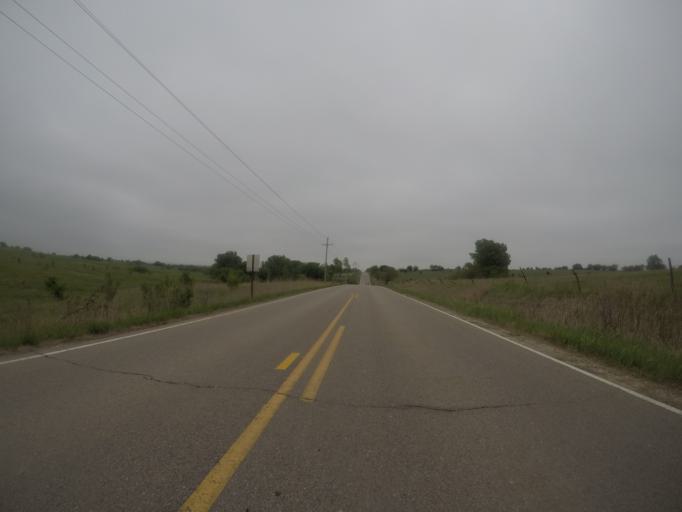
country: US
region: Kansas
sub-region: Pottawatomie County
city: Westmoreland
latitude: 39.5222
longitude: -96.3029
